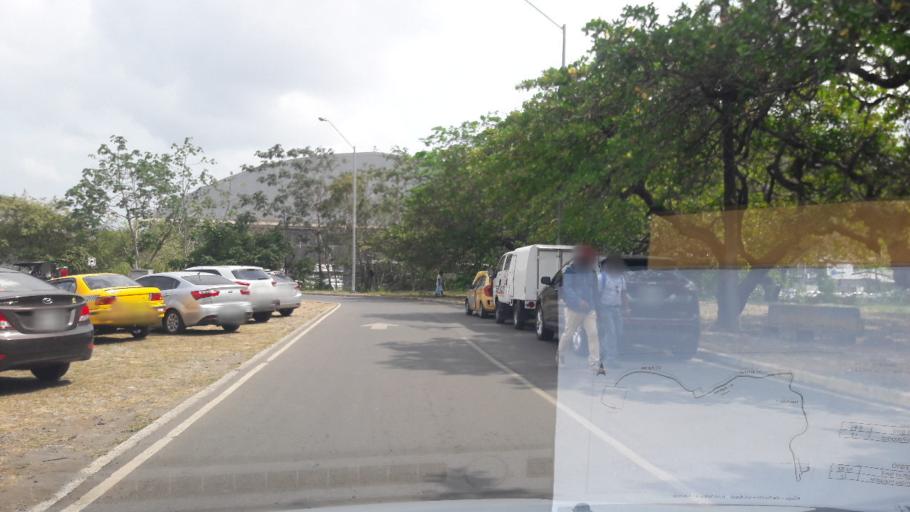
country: PA
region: Panama
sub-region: Distrito de Panama
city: Ancon
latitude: 8.9723
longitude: -79.5494
